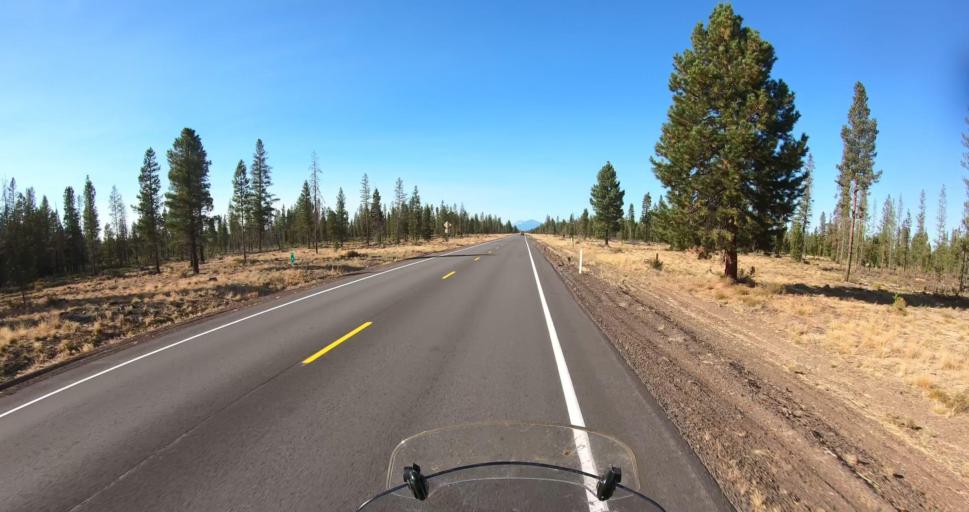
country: US
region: Oregon
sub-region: Deschutes County
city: La Pine
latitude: 43.5663
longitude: -121.4796
